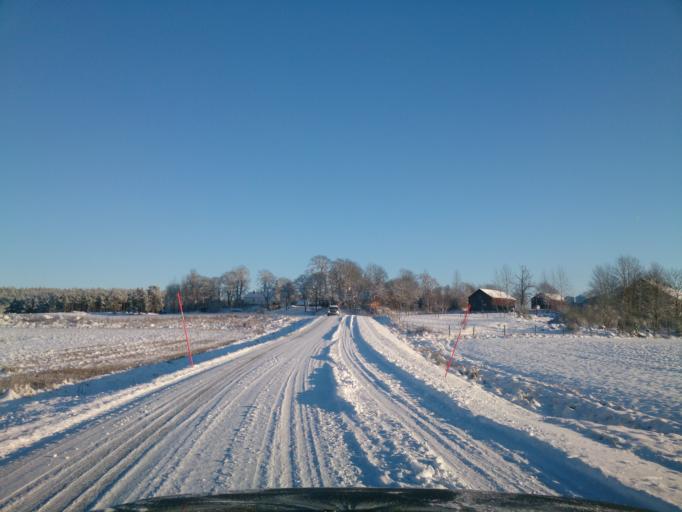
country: SE
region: OEstergoetland
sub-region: Norrkopings Kommun
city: Krokek
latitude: 58.5220
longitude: 16.4973
